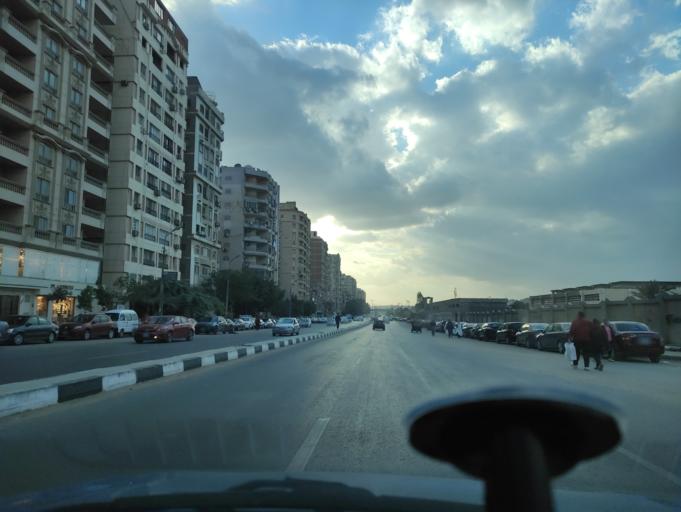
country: EG
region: Muhafazat al Qalyubiyah
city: Al Khankah
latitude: 30.1285
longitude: 31.3728
